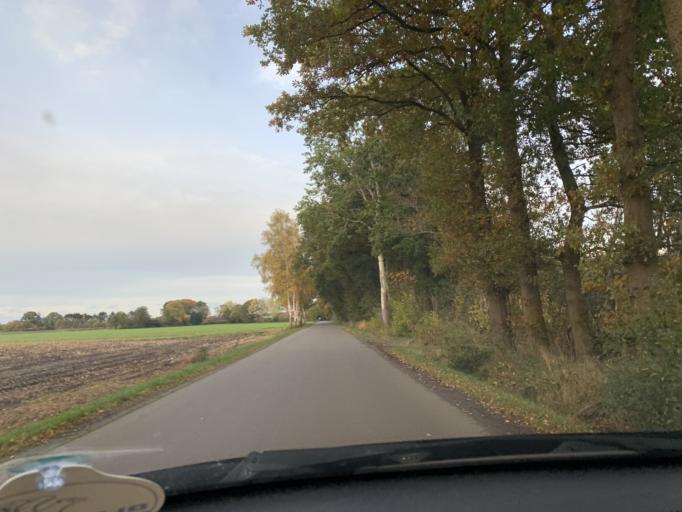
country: DE
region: Lower Saxony
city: Wiefelstede
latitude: 53.2471
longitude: 8.0643
